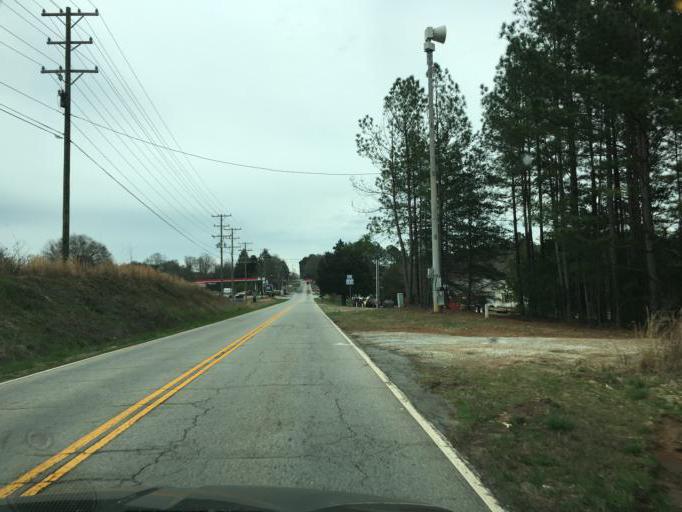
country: US
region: South Carolina
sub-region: Pickens County
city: Central
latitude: 34.8316
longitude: -82.8434
